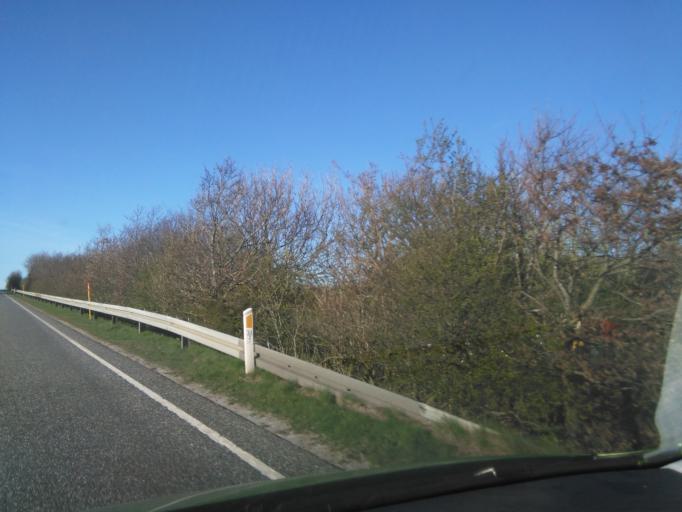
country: DK
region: Central Jutland
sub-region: Ringkobing-Skjern Kommune
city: Videbaek
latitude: 56.0769
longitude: 8.5071
